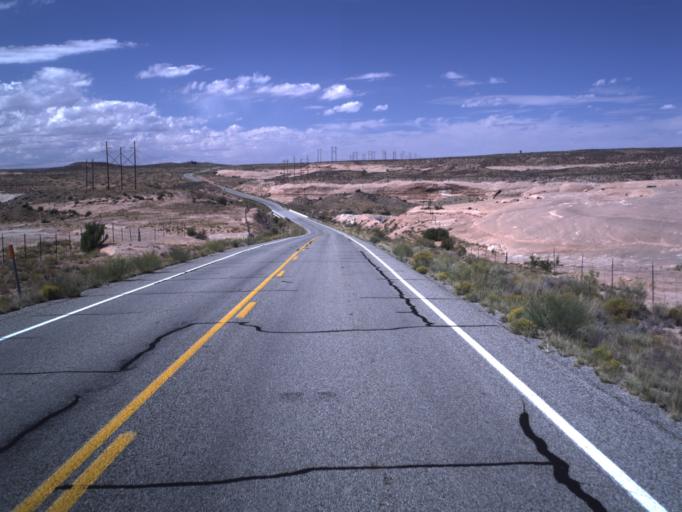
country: US
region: Utah
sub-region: San Juan County
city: Blanding
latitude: 37.3009
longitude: -109.4515
